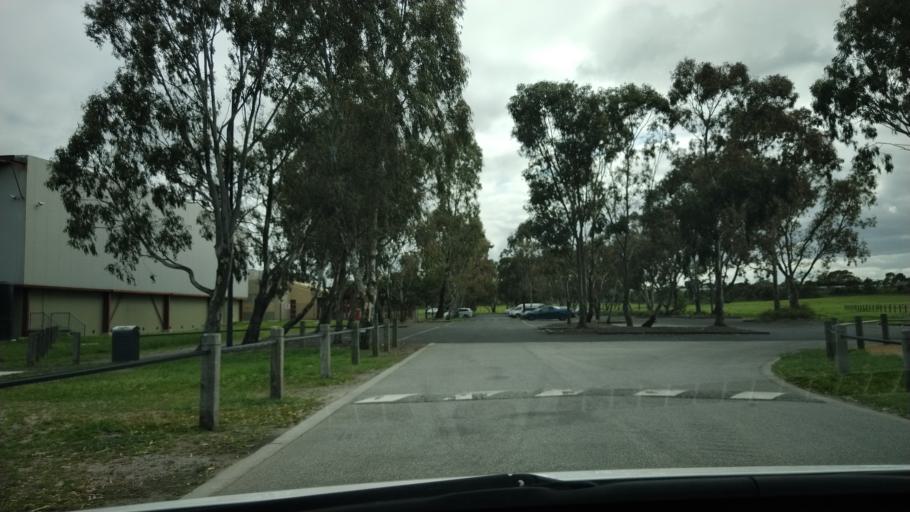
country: AU
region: Victoria
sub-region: Greater Dandenong
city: Keysborough
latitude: -37.9968
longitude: 145.1549
